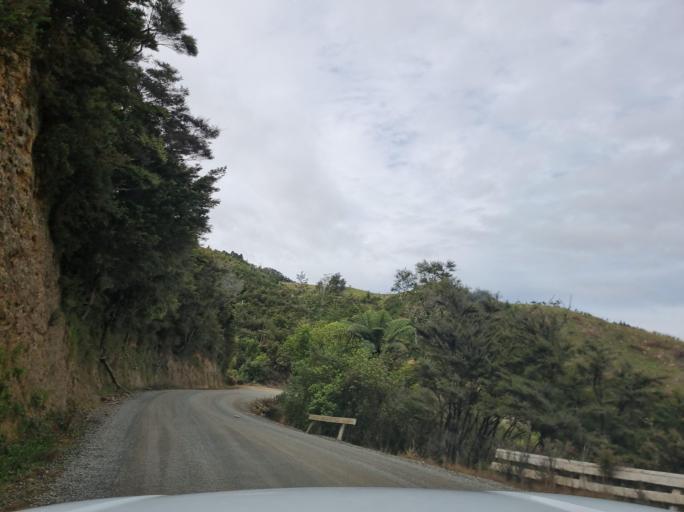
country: NZ
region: Northland
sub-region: Whangarei
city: Ruakaka
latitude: -36.0385
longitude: 174.4113
